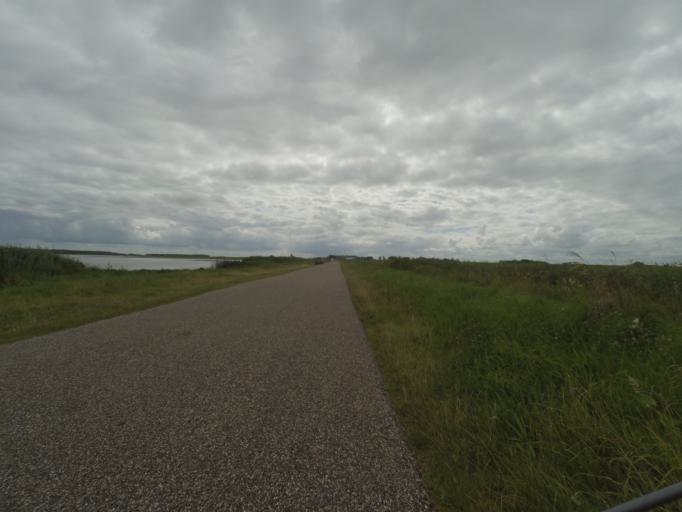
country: NL
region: Friesland
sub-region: Gemeente Dongeradeel
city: Anjum
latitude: 53.3468
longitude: 6.1530
